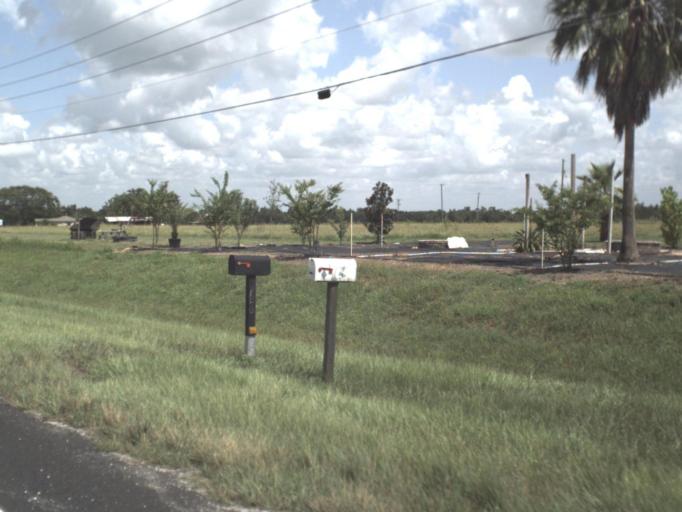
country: US
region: Florida
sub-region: Hardee County
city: Bowling Green
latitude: 27.6111
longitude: -81.8259
